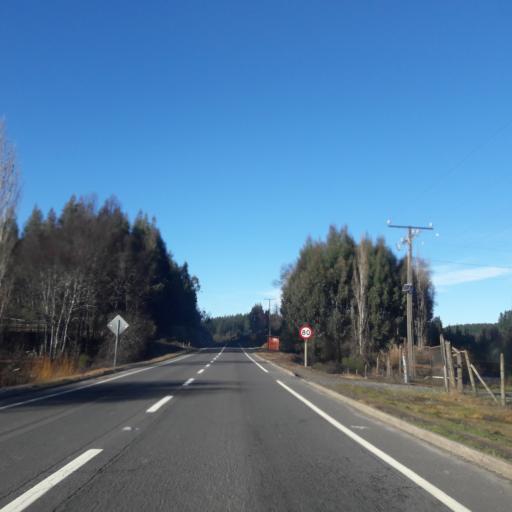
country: CL
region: Biobio
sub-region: Provincia de Biobio
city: La Laja
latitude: -37.2775
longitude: -72.9479
